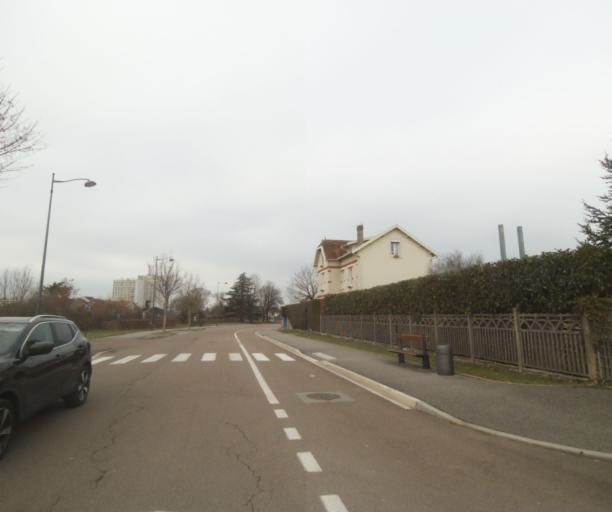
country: FR
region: Champagne-Ardenne
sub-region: Departement de la Haute-Marne
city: Bettancourt-la-Ferree
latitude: 48.6384
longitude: 4.9638
